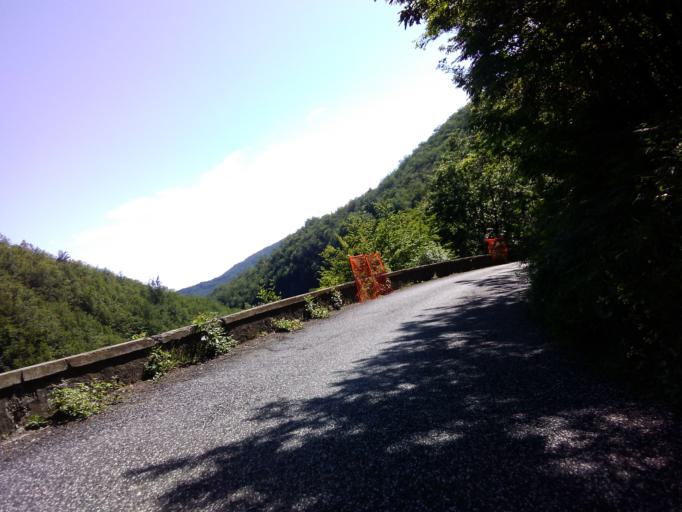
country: IT
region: Tuscany
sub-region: Provincia di Massa-Carrara
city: Comano
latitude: 44.3201
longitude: 10.0945
